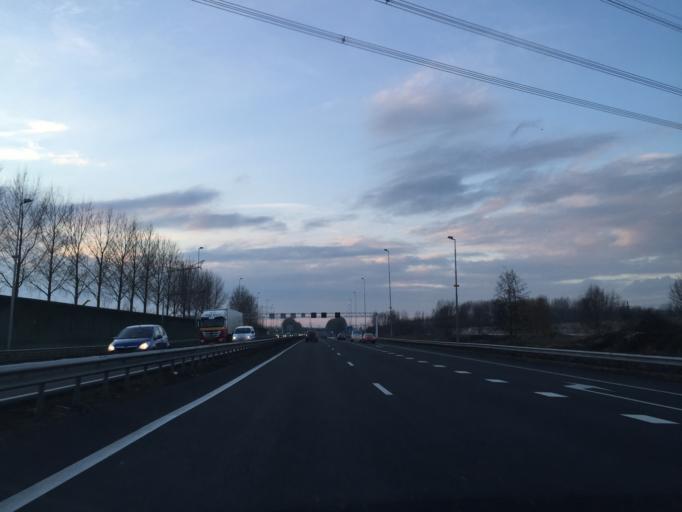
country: NL
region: South Holland
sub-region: Gemeente Papendrecht
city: Papendrecht
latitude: 51.8366
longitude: 4.7237
